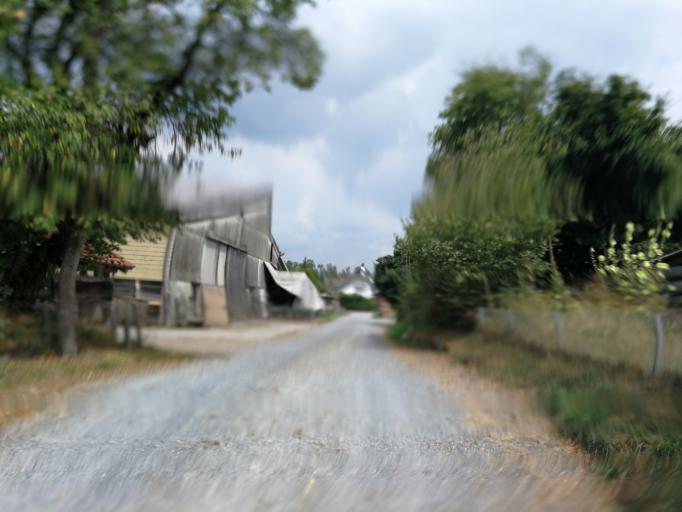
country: CH
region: Zurich
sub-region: Bezirk Hinwil
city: Binzikon
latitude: 47.2761
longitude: 8.7600
